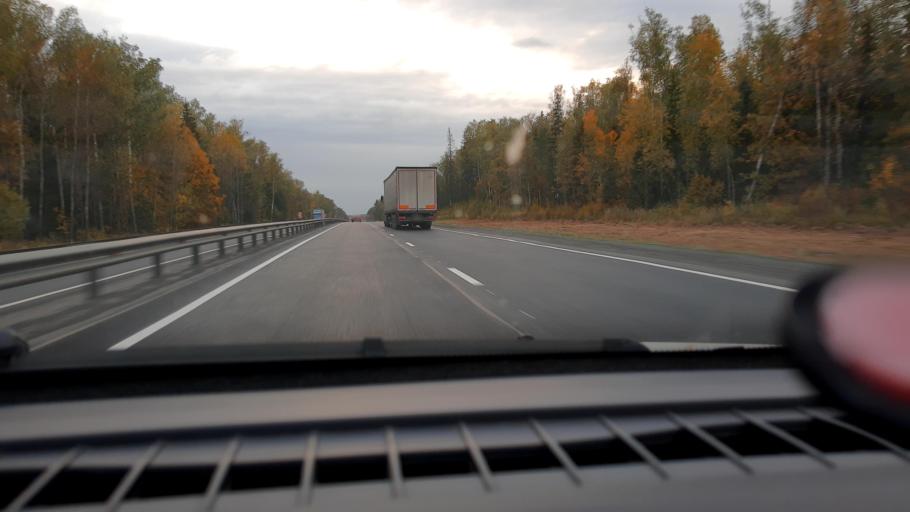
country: RU
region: Vladimir
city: Kameshkovo
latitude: 56.1996
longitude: 41.0602
